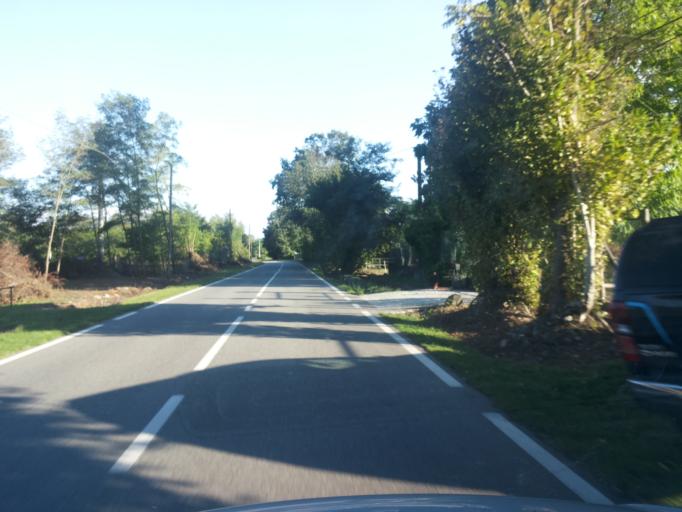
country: IT
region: Piedmont
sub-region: Provincia di Vercelli
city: Borgo d'Ale
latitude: 45.3683
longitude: 8.0325
